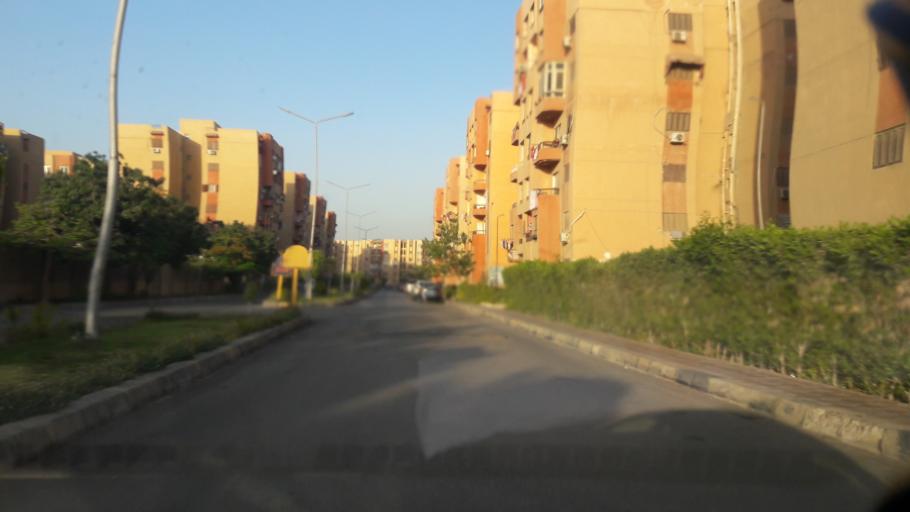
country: EG
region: Al Jizah
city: Madinat Sittah Uktubar
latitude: 29.9553
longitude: 31.0427
